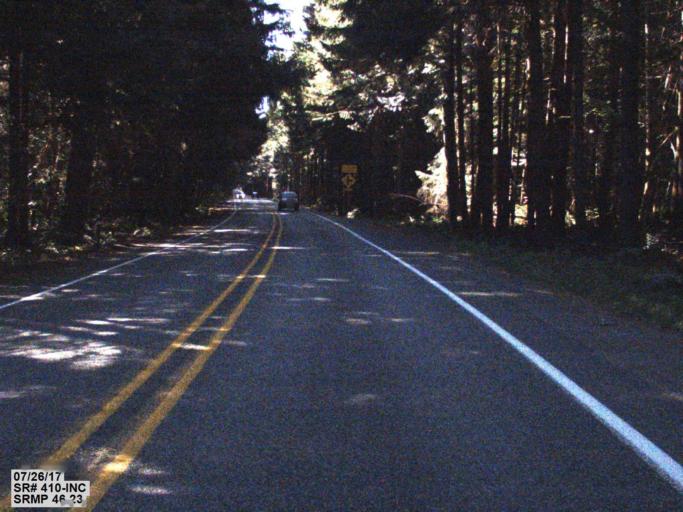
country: US
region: Washington
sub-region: King County
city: Riverbend
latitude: 47.1207
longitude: -121.6120
